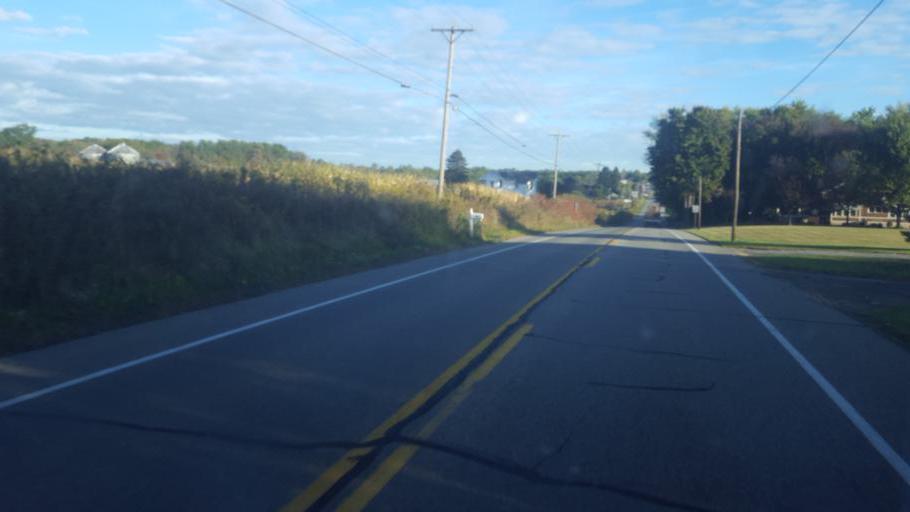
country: US
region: Pennsylvania
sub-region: Mercer County
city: Mercer
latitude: 41.2122
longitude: -80.2397
